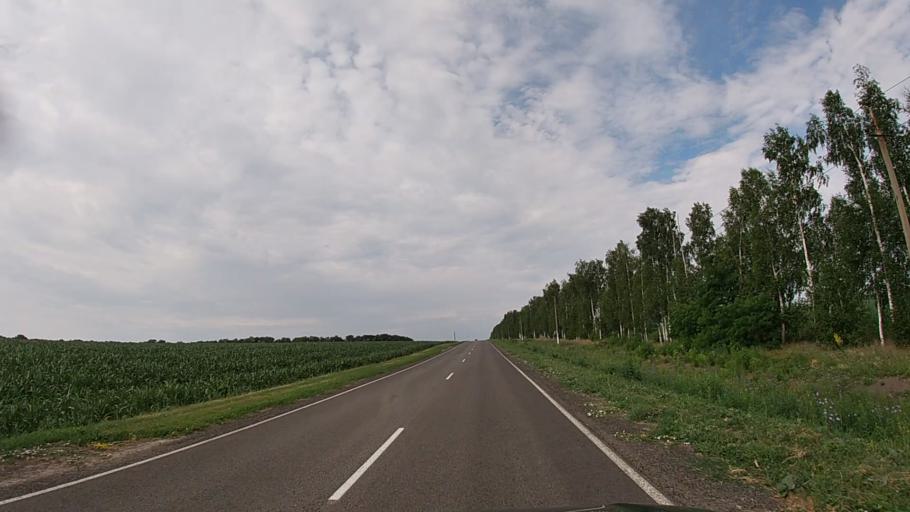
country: RU
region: Belgorod
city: Krasnaya Yaruga
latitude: 50.8223
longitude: 35.4613
